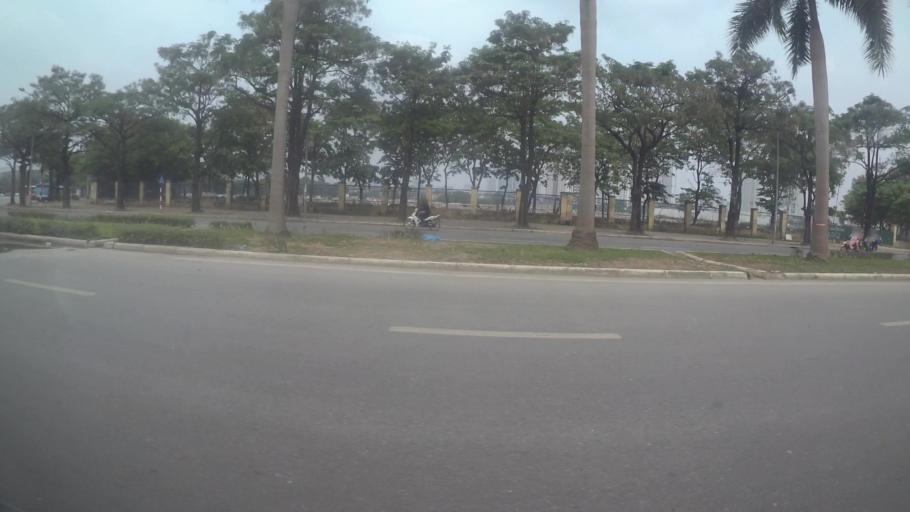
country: VN
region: Ha Noi
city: Cau Dien
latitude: 21.0187
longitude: 105.7669
